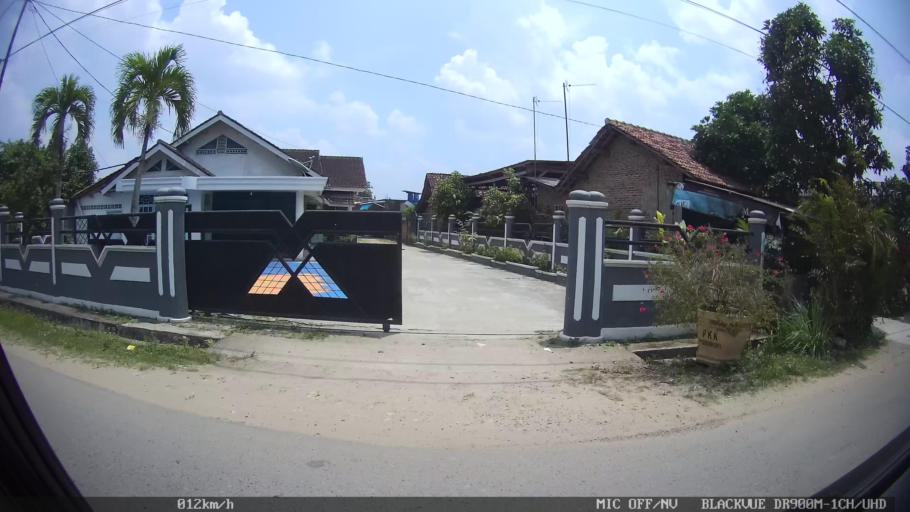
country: ID
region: Lampung
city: Pringsewu
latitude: -5.3484
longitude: 104.9875
